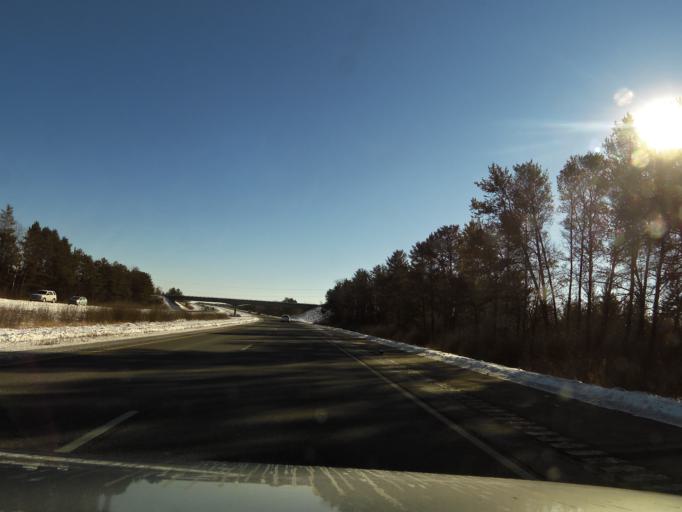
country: US
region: Wisconsin
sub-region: Jackson County
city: Black River Falls
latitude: 44.2791
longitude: -90.8057
